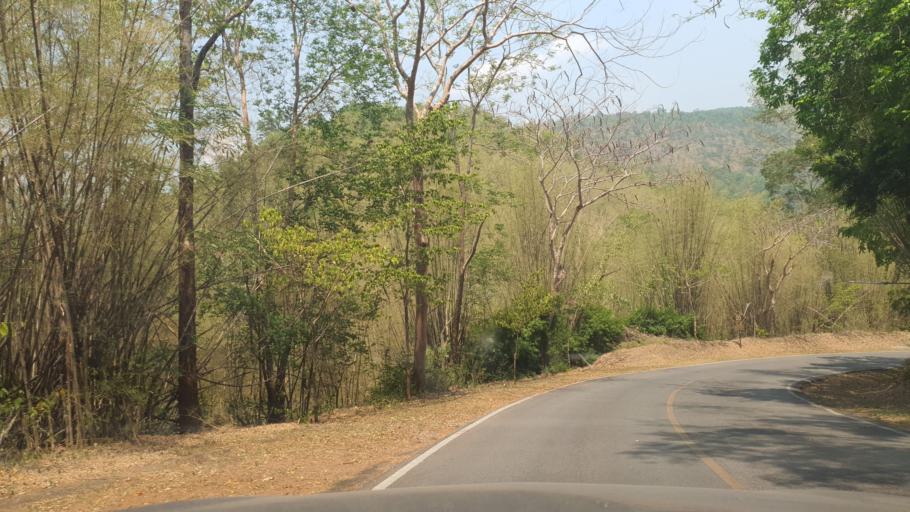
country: TH
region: Kanchanaburi
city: Si Sawat
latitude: 14.3798
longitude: 99.1408
